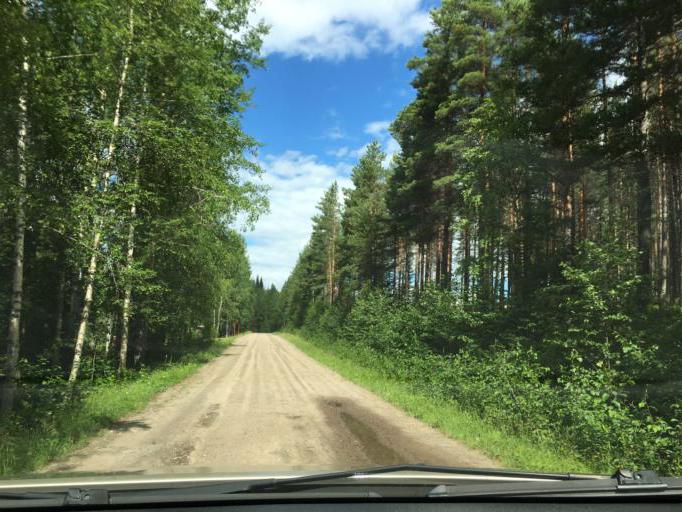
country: SE
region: Norrbotten
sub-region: Overkalix Kommun
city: OEverkalix
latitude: 66.1299
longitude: 22.7846
